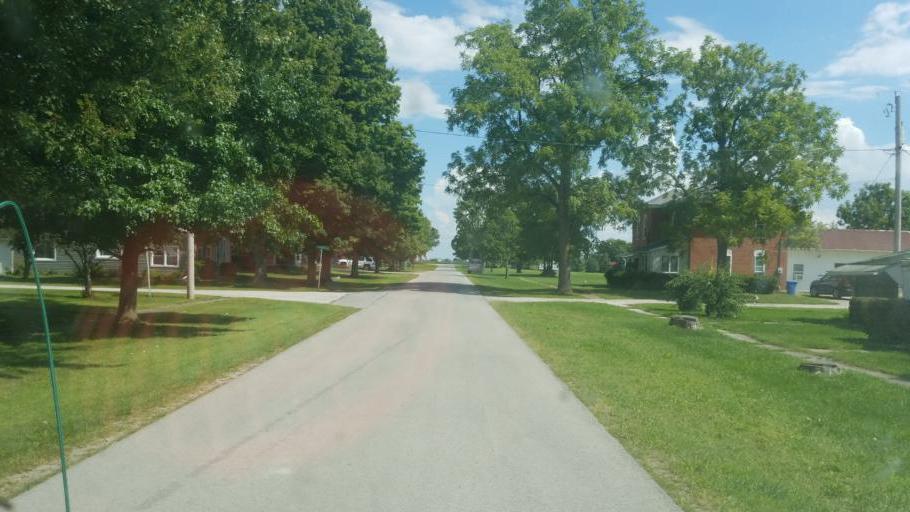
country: US
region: Ohio
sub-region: Hardin County
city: Forest
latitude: 40.8603
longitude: -83.4603
